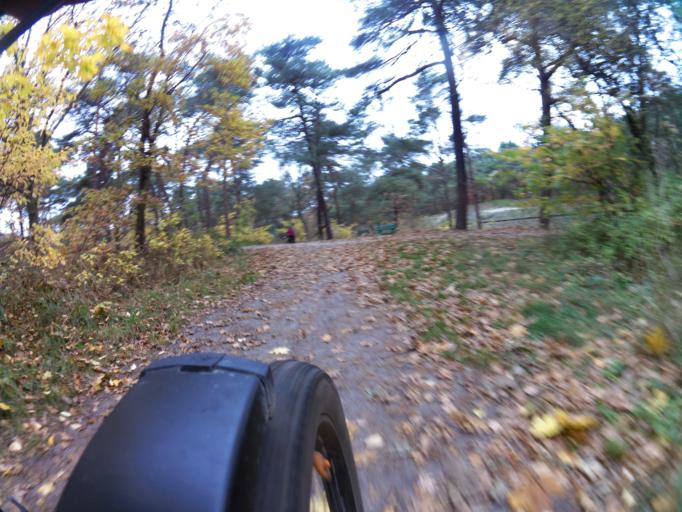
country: PL
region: Pomeranian Voivodeship
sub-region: Powiat pucki
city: Jastarnia
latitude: 54.6963
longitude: 18.6898
